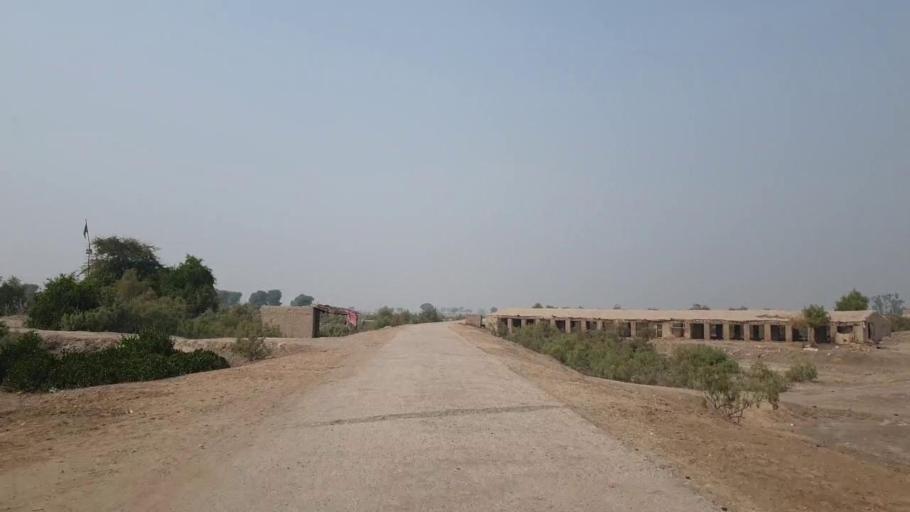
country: PK
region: Sindh
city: Bhan
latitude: 26.5049
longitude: 67.6913
